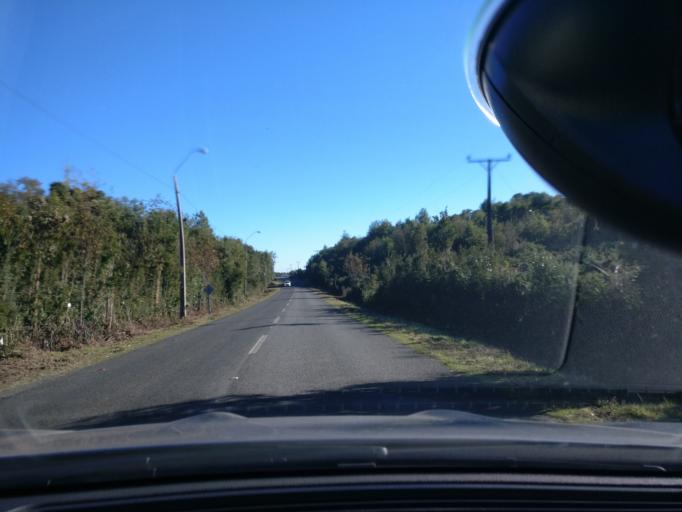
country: CL
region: Los Lagos
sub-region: Provincia de Chiloe
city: Castro
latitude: -42.3178
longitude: -73.3774
